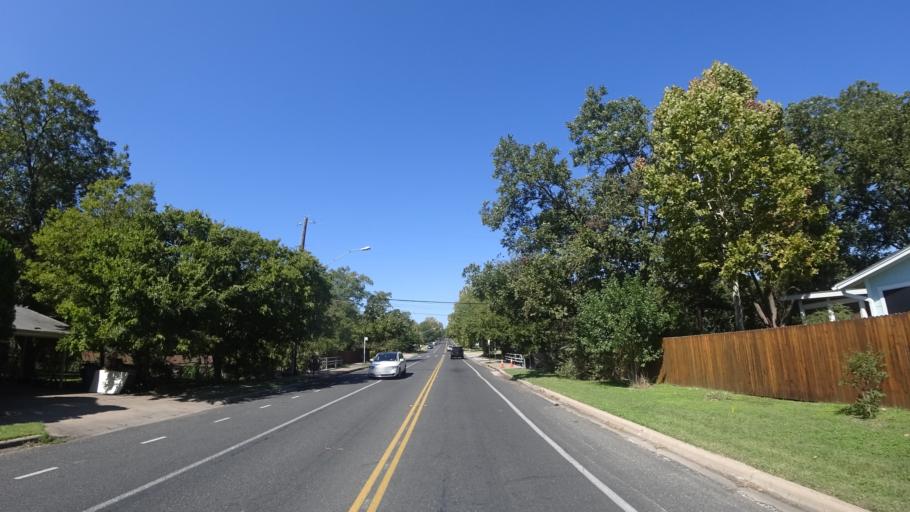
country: US
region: Texas
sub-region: Travis County
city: Austin
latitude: 30.3148
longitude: -97.6939
